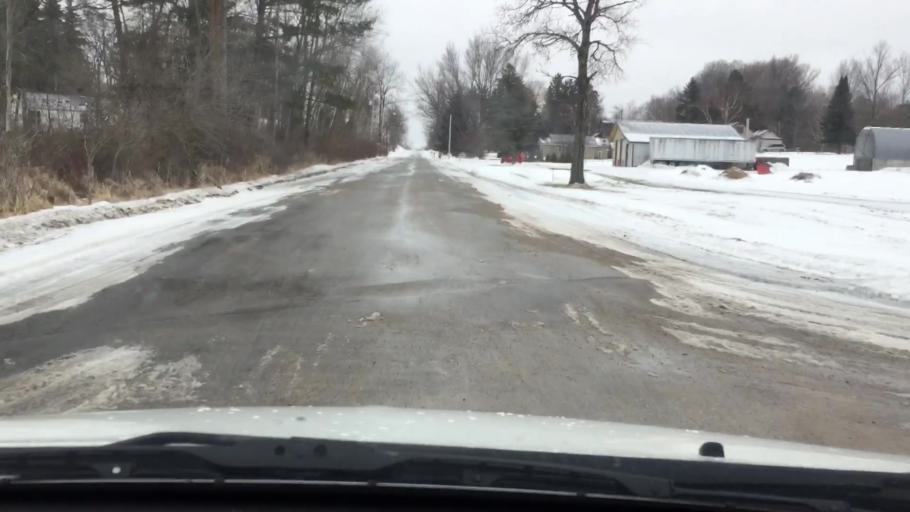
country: US
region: Michigan
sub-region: Osceola County
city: Reed City
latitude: 44.0359
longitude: -85.4538
